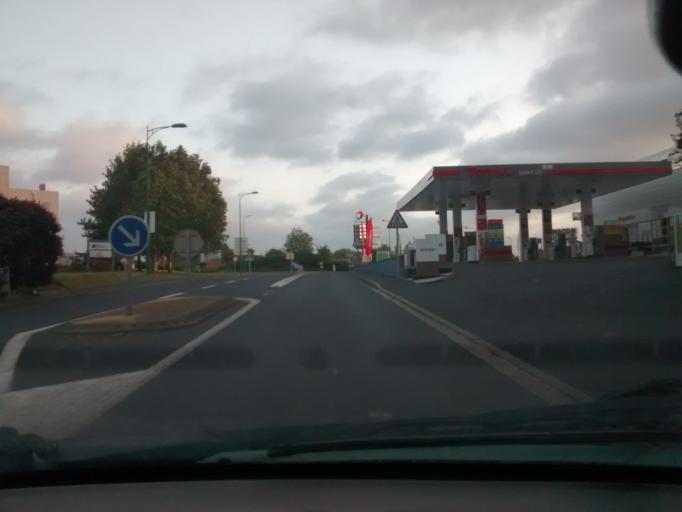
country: FR
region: Lower Normandy
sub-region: Departement de la Manche
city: Agneaux
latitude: 49.1024
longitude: -1.1147
